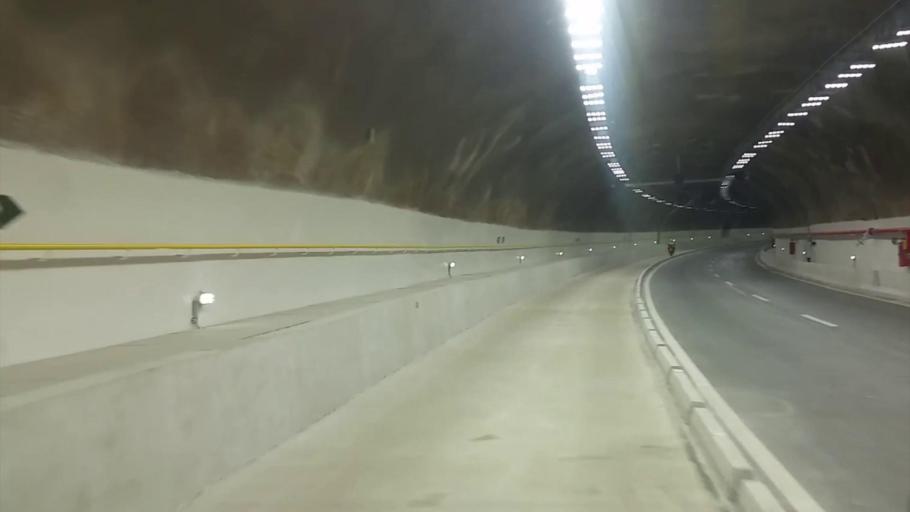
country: BR
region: Rio de Janeiro
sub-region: Nilopolis
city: Nilopolis
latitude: -22.8996
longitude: -43.3980
